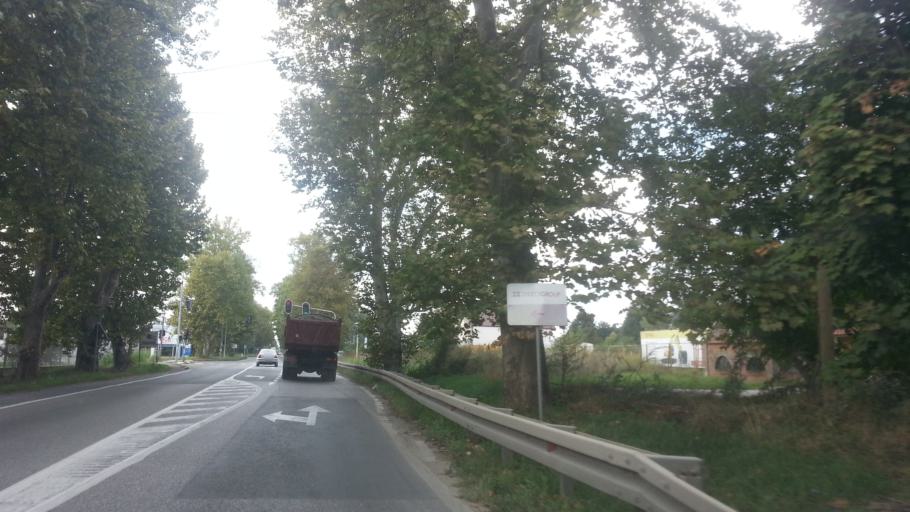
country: RS
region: Central Serbia
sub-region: Belgrade
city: Zemun
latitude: 44.8677
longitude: 20.3581
